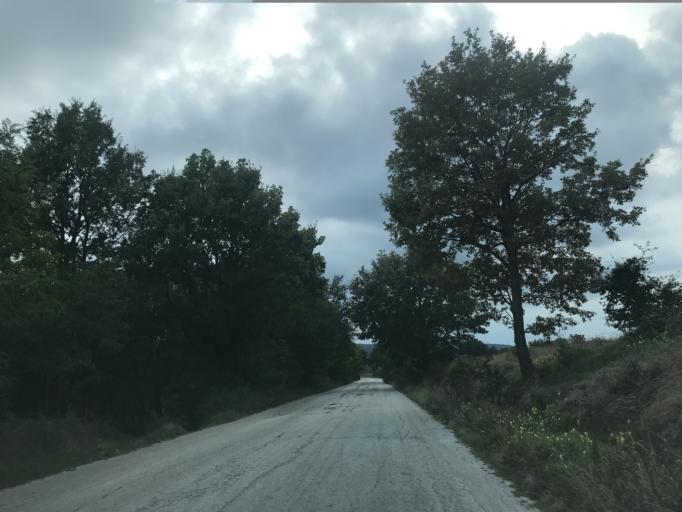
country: IT
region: Molise
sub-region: Provincia di Isernia
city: Bagnoli del Trigno
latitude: 41.6820
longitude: 14.4548
